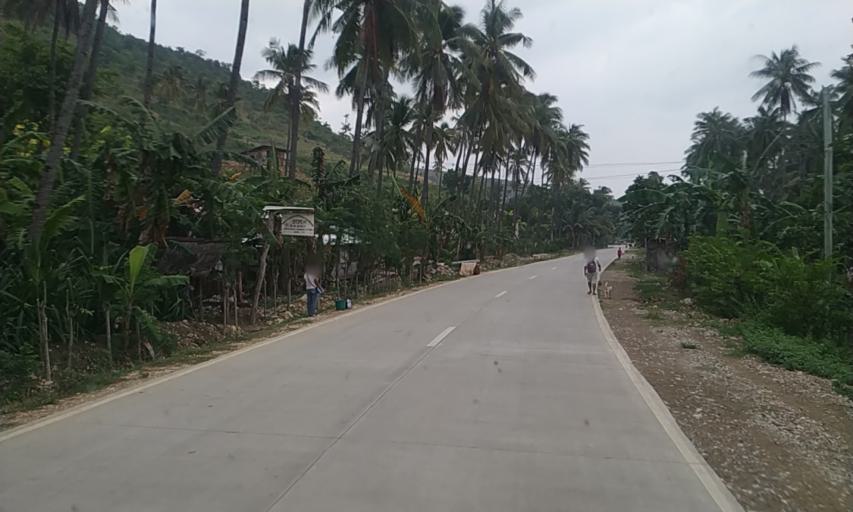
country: PH
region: Central Visayas
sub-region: Province of Negros Oriental
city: Calamba
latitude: 10.1917
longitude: 123.2942
